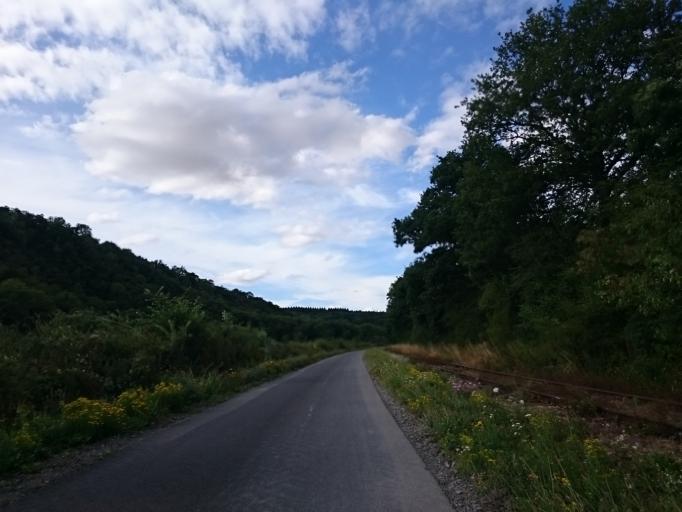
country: FR
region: Lower Normandy
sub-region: Departement du Calvados
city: Sainte-Honorine-du-Fay
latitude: 49.0585
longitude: -0.4597
